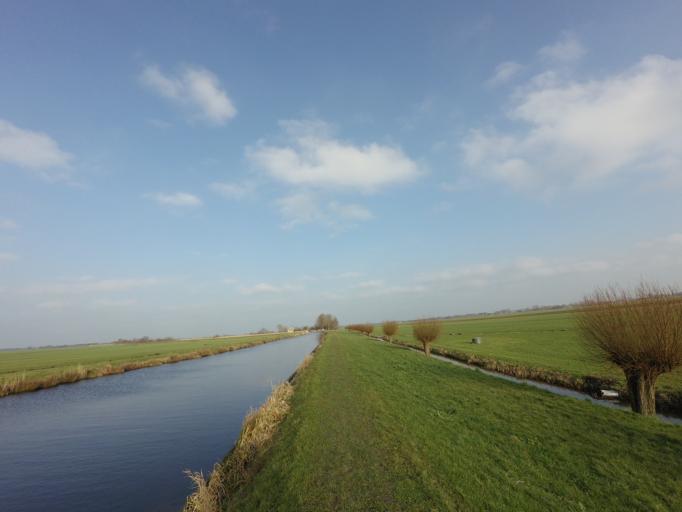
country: NL
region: Utrecht
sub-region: Gemeente Woerden
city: Woerden
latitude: 52.1001
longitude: 4.8680
